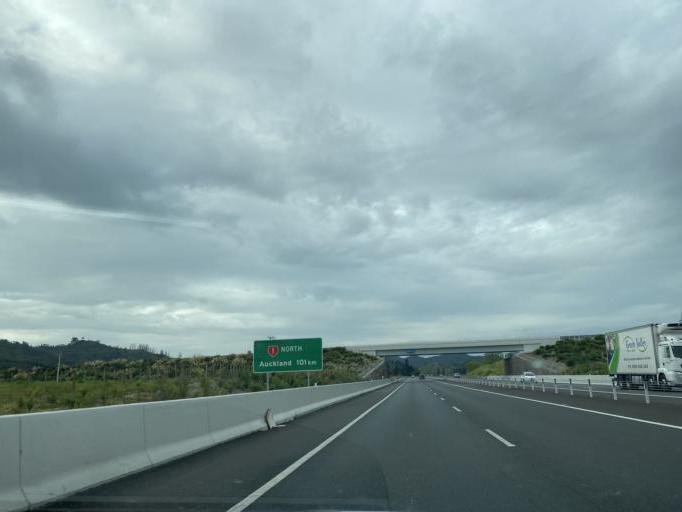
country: NZ
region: Waikato
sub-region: Waikato District
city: Ngaruawahia
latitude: -37.6134
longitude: 175.2047
